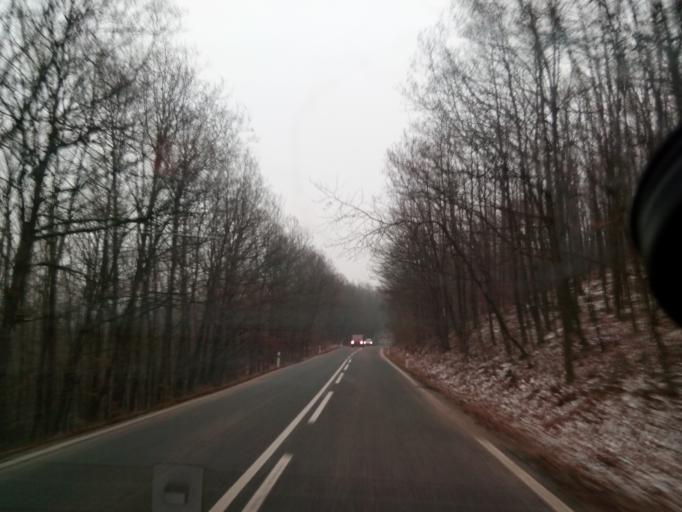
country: SK
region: Kosicky
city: Kosice
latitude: 48.7115
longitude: 21.1943
